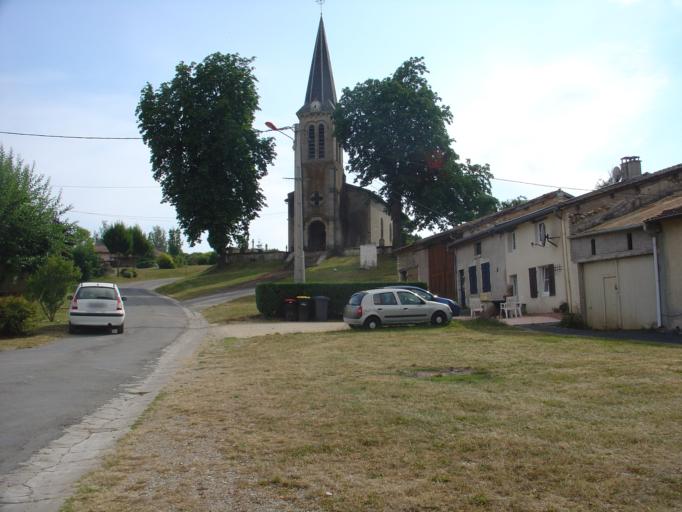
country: FR
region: Lorraine
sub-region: Departement de la Meuse
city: Dieue-sur-Meuse
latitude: 48.9389
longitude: 5.4091
